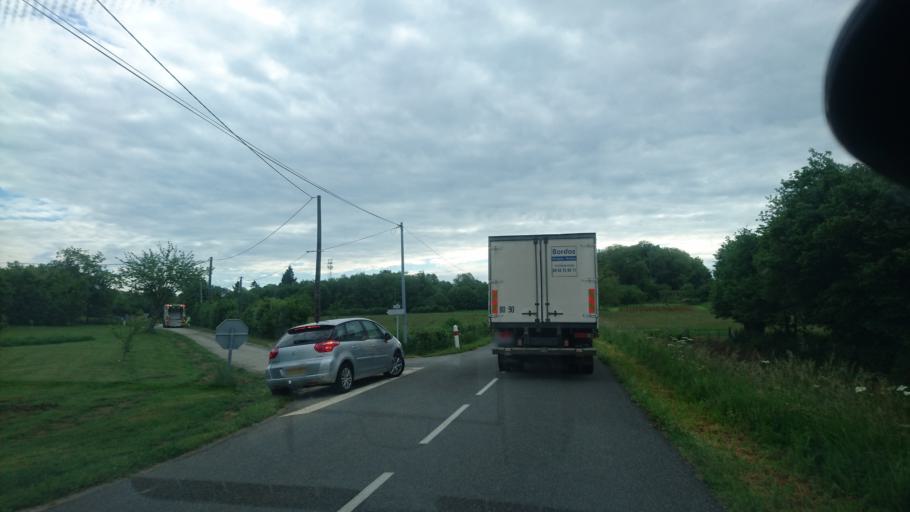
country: FR
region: Limousin
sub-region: Departement de la Haute-Vienne
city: Linards
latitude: 45.6556
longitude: 1.5517
